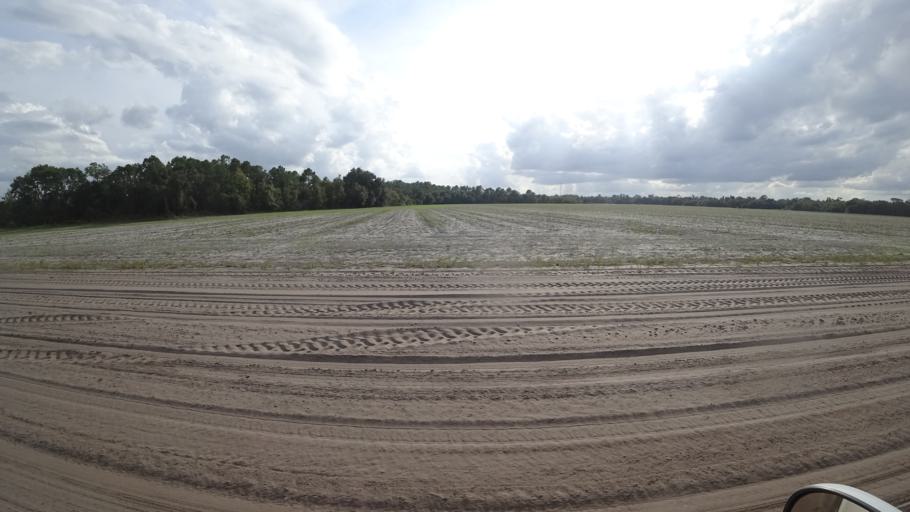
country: US
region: Florida
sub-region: Hillsborough County
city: Wimauma
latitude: 27.6073
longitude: -82.1447
